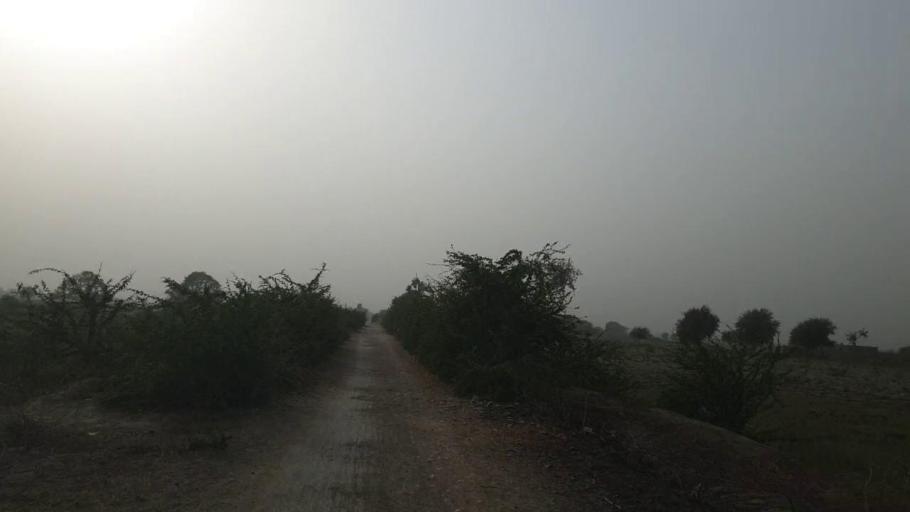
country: PK
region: Sindh
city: Kunri
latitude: 25.0669
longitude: 69.4563
